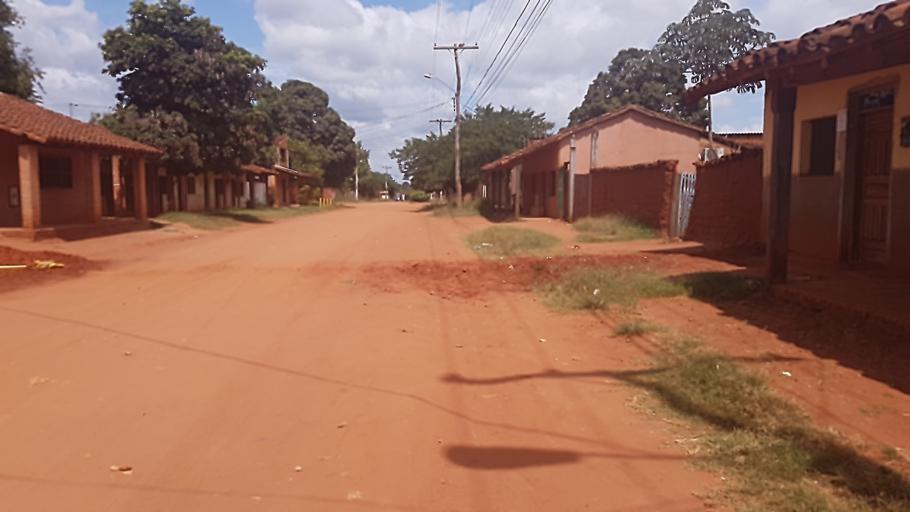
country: BO
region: Santa Cruz
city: San Ignacio de Velasco
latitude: -16.3746
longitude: -60.9650
